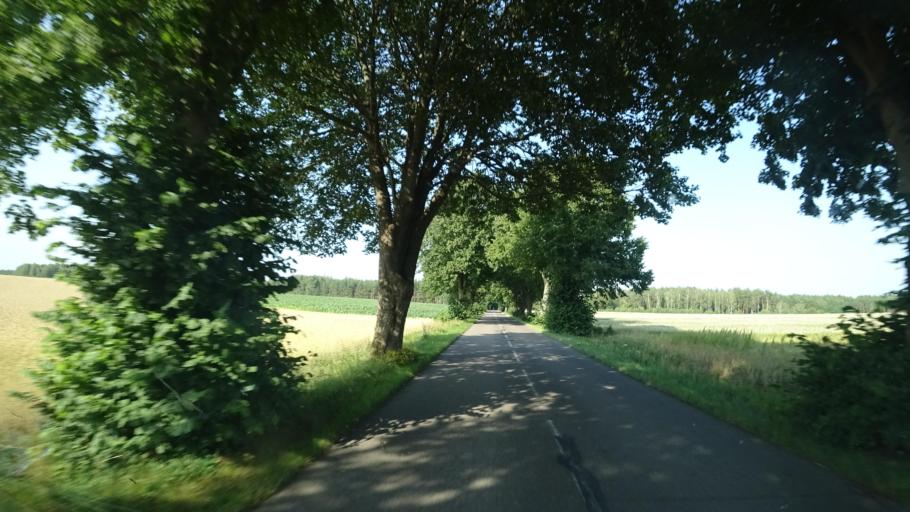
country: PL
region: Pomeranian Voivodeship
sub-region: Powiat czluchowski
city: Rzeczenica
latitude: 53.7635
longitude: 17.1385
